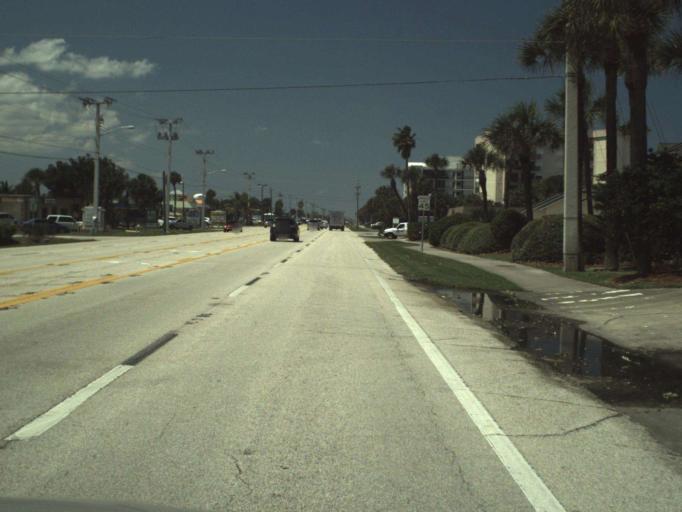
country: US
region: Florida
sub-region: Brevard County
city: Satellite Beach
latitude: 28.1726
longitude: -80.5894
